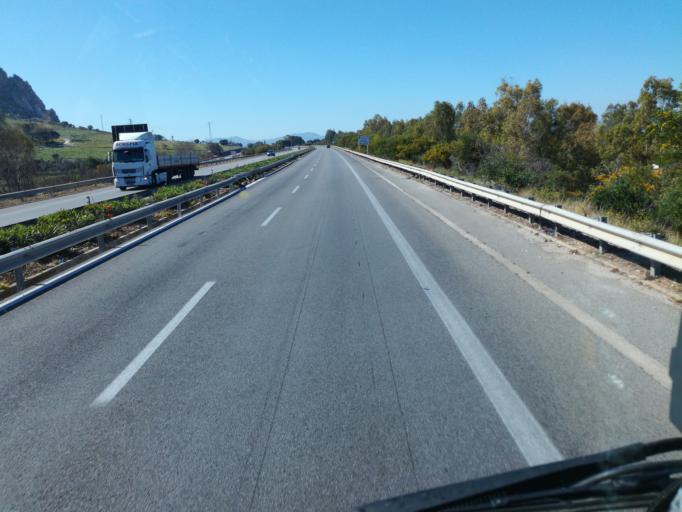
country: IT
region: Sicily
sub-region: Palermo
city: Agliandroni-Paternella
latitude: 38.1329
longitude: 13.0751
